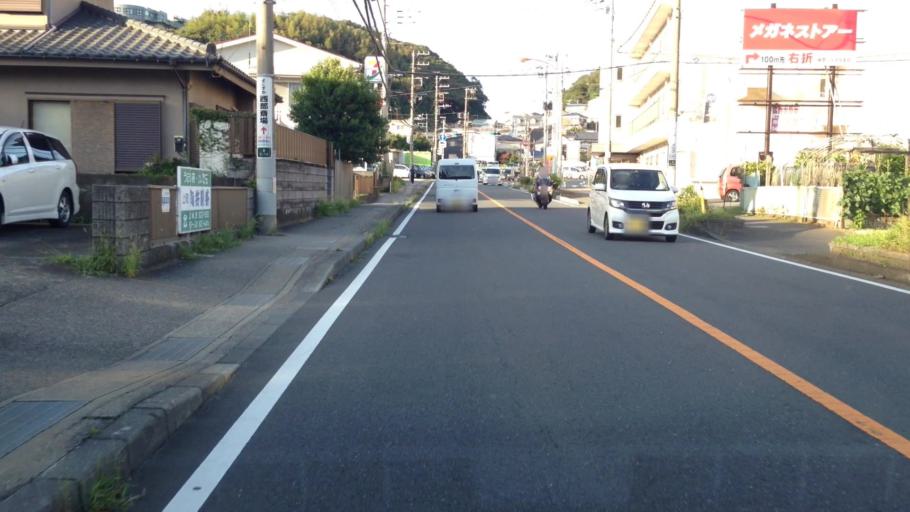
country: JP
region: Kanagawa
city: Yokosuka
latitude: 35.2288
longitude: 139.6519
